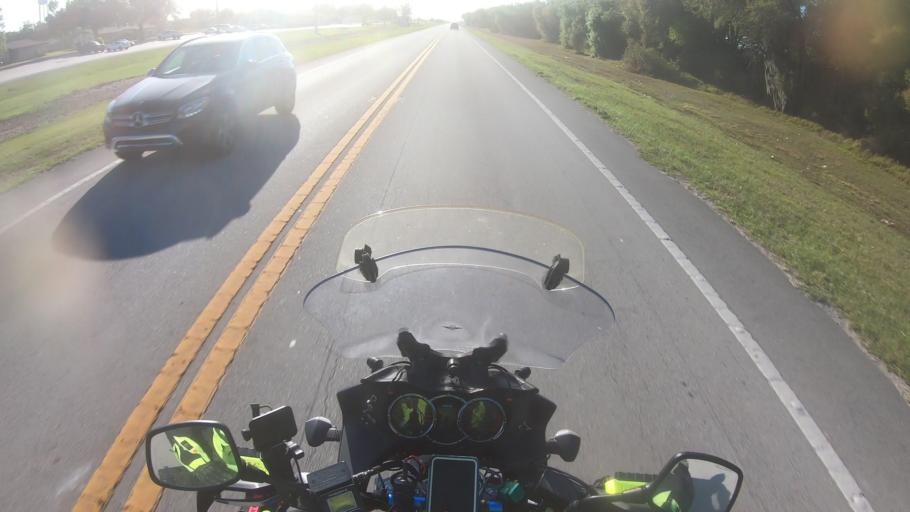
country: US
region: Florida
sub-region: DeSoto County
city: Southeast Arcadia
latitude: 27.2106
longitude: -81.6679
